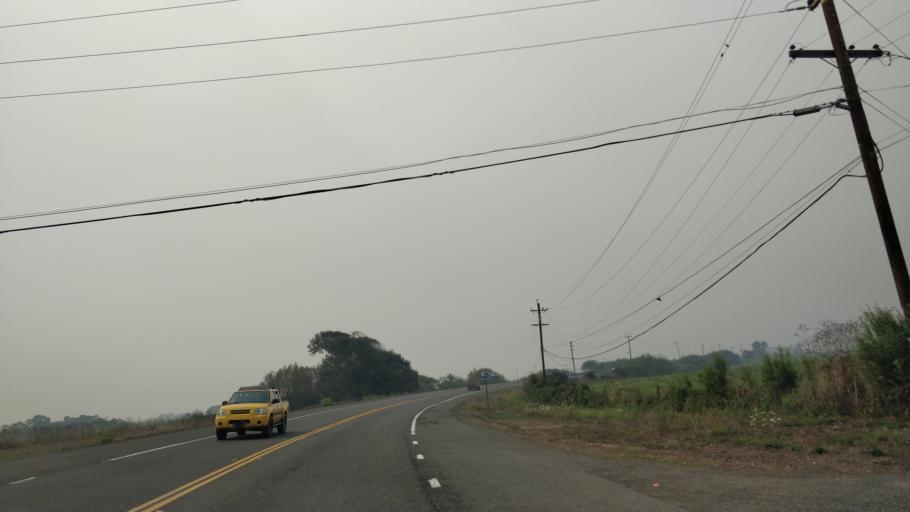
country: US
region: California
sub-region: Humboldt County
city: Ferndale
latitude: 40.5997
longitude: -124.2141
